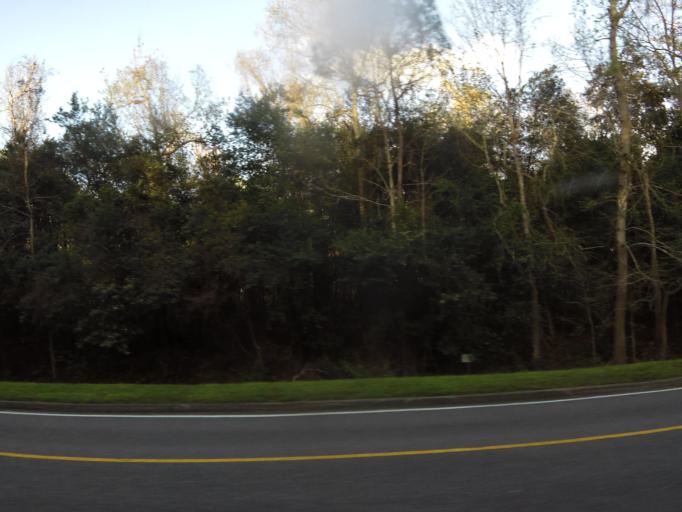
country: US
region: Florida
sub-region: Duval County
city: Jacksonville Beach
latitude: 30.2647
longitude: -81.5104
